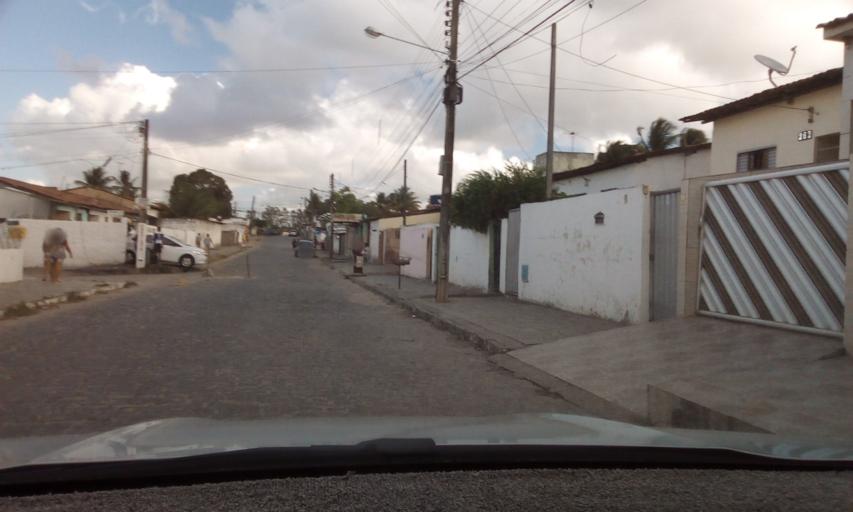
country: BR
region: Paraiba
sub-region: Bayeux
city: Bayeux
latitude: -7.1697
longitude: -34.9138
